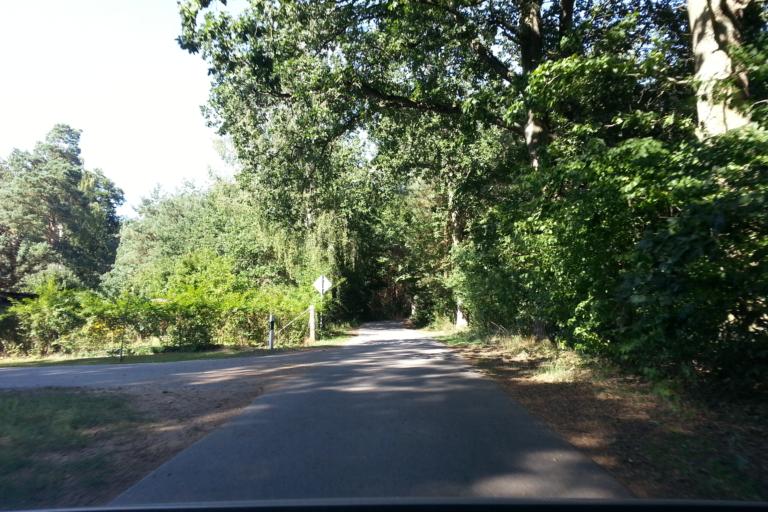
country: DE
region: Mecklenburg-Vorpommern
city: Torgelow
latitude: 53.6530
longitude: 14.0297
